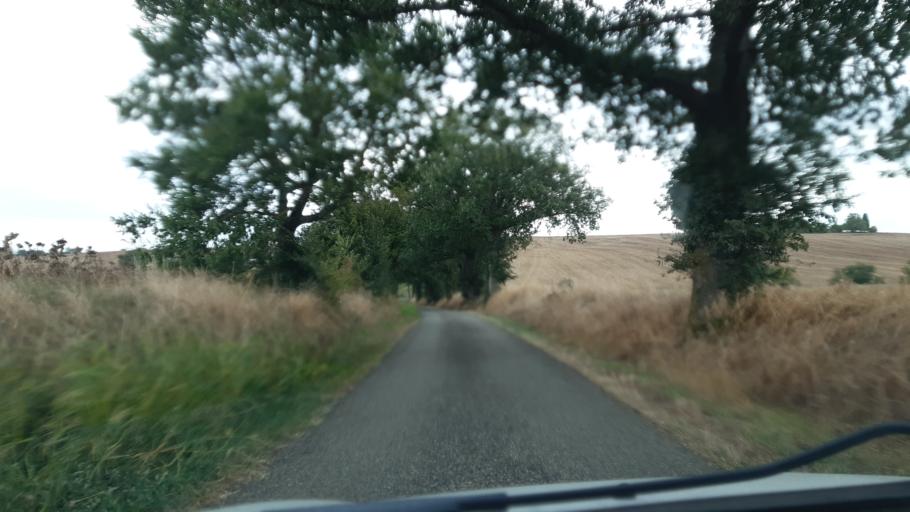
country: FR
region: Midi-Pyrenees
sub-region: Departement du Gers
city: Gimont
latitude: 43.6704
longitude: 0.9849
